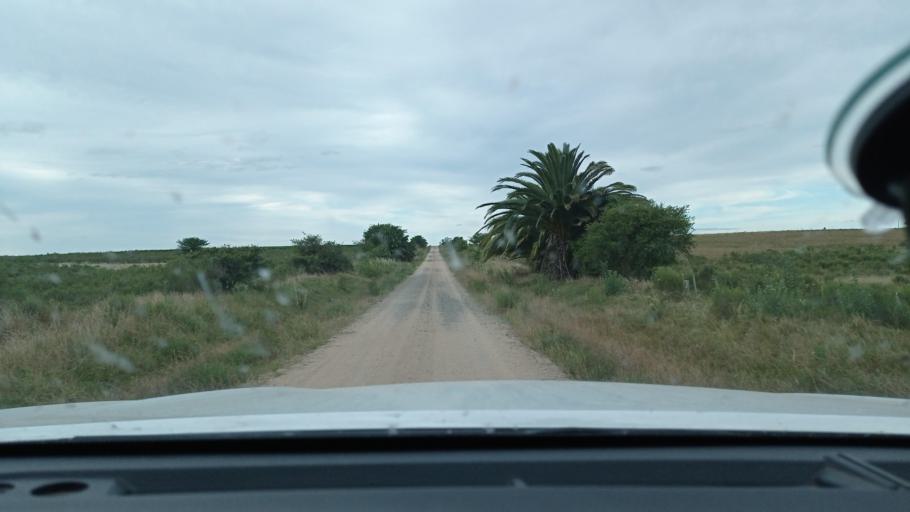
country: UY
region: Florida
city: Casupa
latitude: -34.1356
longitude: -55.7822
